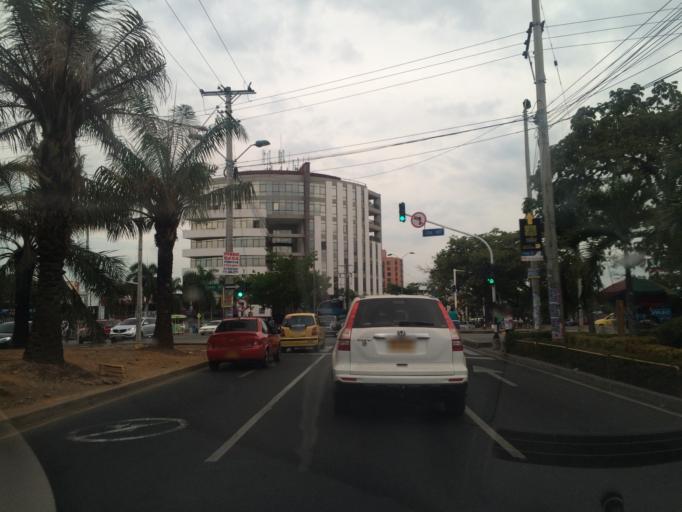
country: CO
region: Valle del Cauca
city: Cali
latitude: 3.3679
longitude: -76.5297
